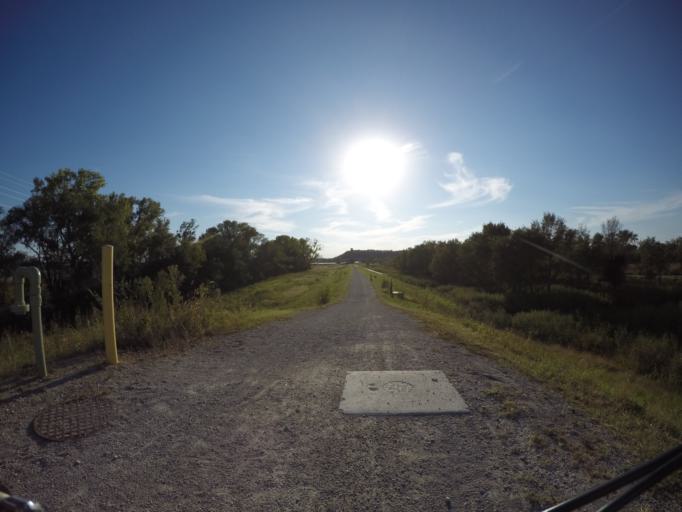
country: US
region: Kansas
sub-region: Riley County
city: Manhattan
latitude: 39.1968
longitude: -96.5475
